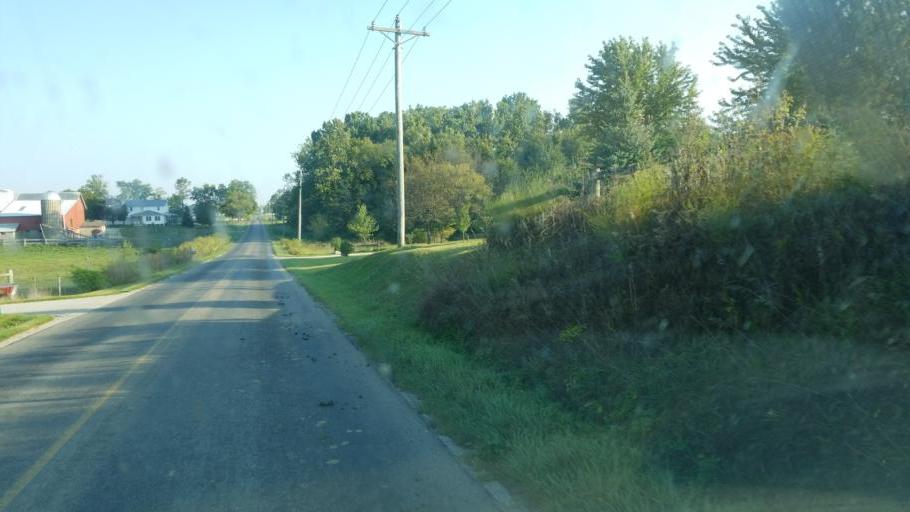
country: US
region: Indiana
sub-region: LaGrange County
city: Lagrange
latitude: 41.5800
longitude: -85.4239
